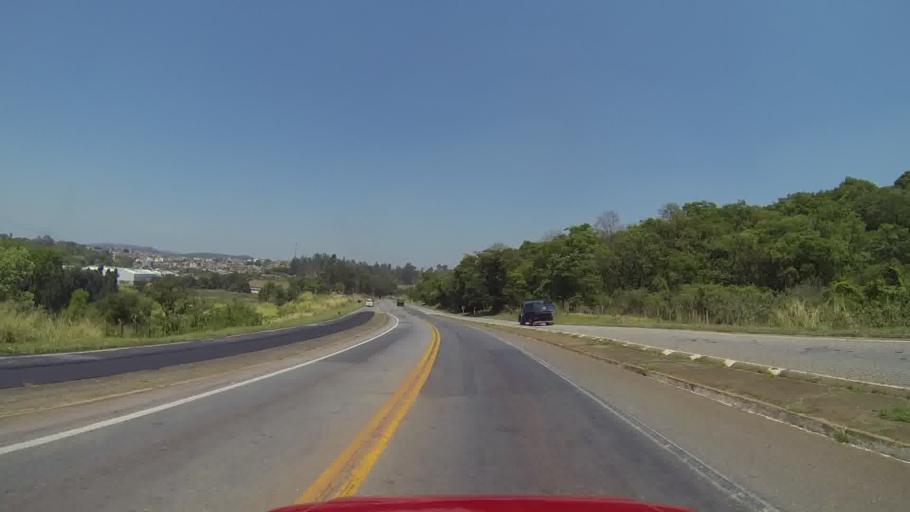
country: BR
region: Minas Gerais
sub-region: Itauna
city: Itauna
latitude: -20.0600
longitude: -44.6021
